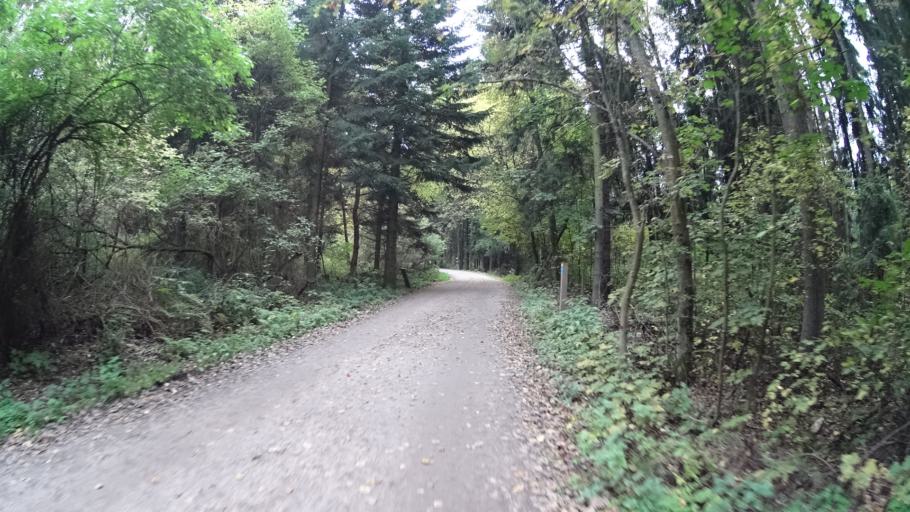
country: FI
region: Uusimaa
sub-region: Helsinki
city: Vantaa
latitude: 60.2180
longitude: 25.0086
